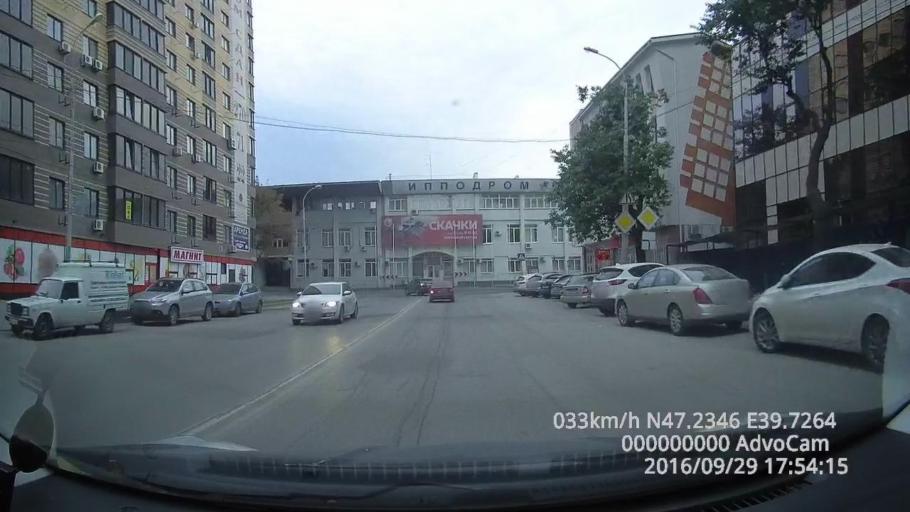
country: RU
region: Rostov
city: Rostov-na-Donu
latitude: 47.2348
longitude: 39.7263
